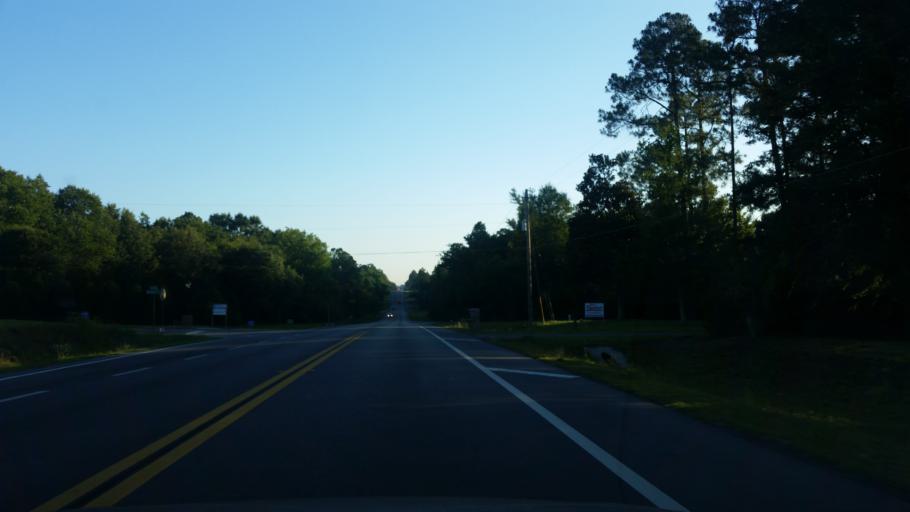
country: US
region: Florida
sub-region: Escambia County
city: Gonzalez
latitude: 30.5594
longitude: -87.3289
